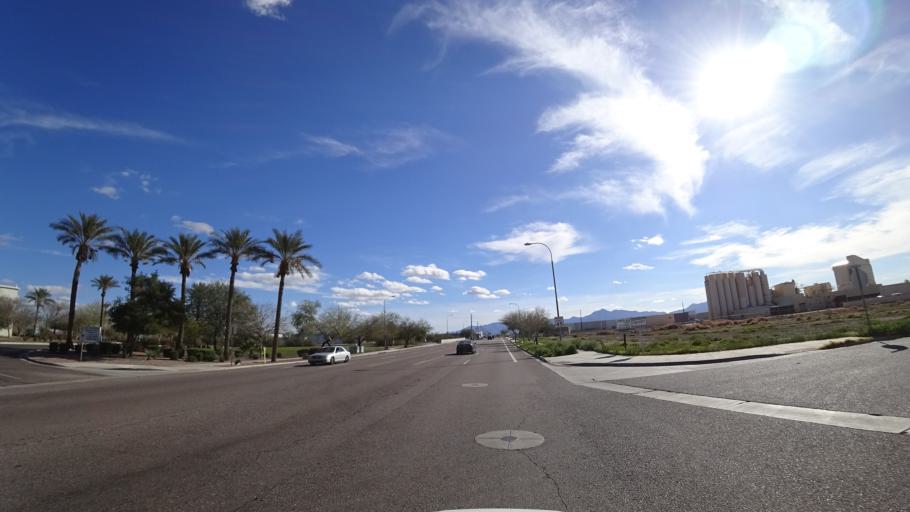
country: US
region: Arizona
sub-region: Maricopa County
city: Tolleson
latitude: 33.4468
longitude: -112.2212
